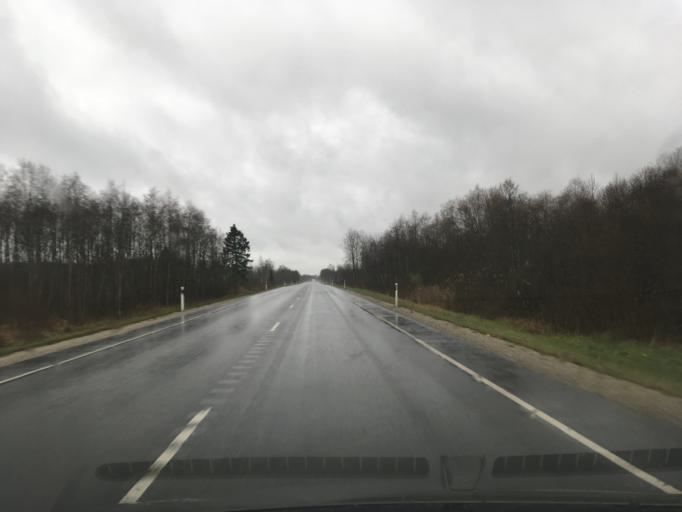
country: EE
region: Laeaene
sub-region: Lihula vald
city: Lihula
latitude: 58.8069
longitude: 24.0494
